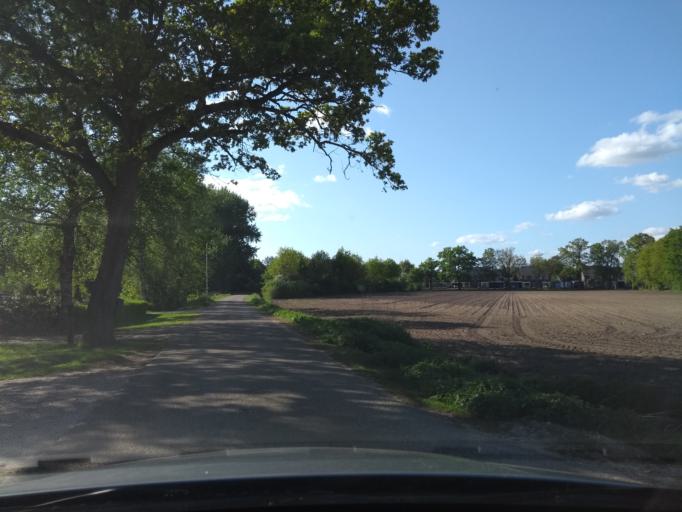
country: NL
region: Overijssel
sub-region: Gemeente Almelo
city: Almelo
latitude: 52.3815
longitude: 6.7166
